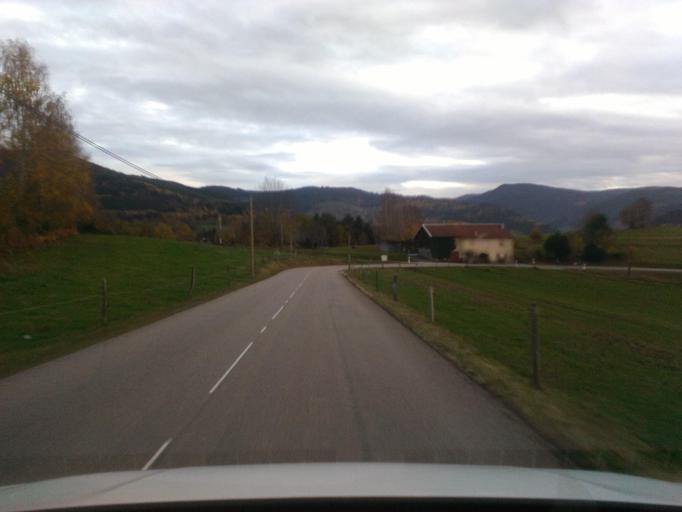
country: FR
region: Lorraine
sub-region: Departement des Vosges
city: Plainfaing
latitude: 48.1927
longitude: 7.0175
